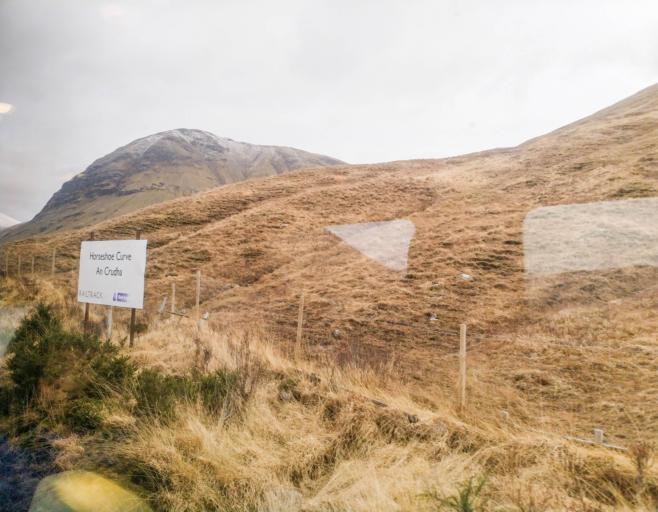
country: GB
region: Scotland
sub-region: Argyll and Bute
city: Garelochhead
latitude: 56.4776
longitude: -4.7165
